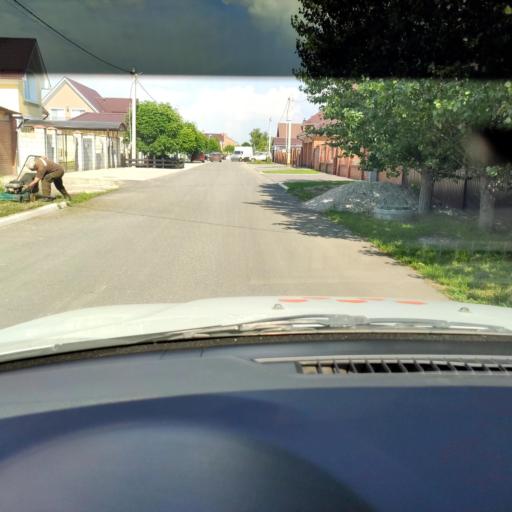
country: RU
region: Samara
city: Podstepki
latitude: 53.5103
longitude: 49.1427
